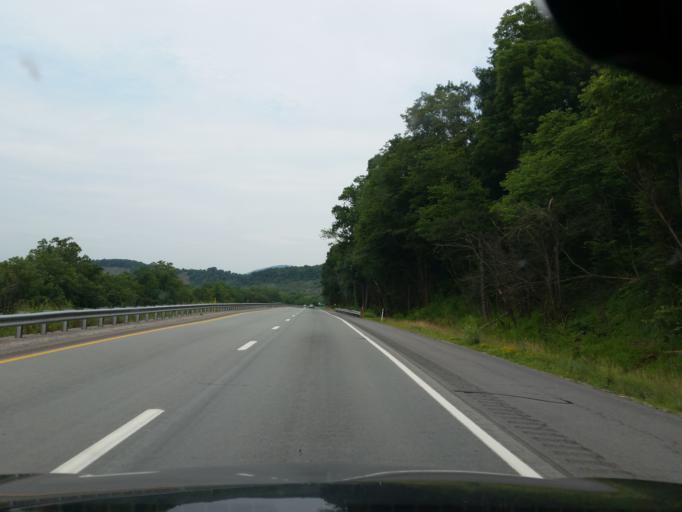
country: US
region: Pennsylvania
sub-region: Perry County
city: Duncannon
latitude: 40.4755
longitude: -77.0373
